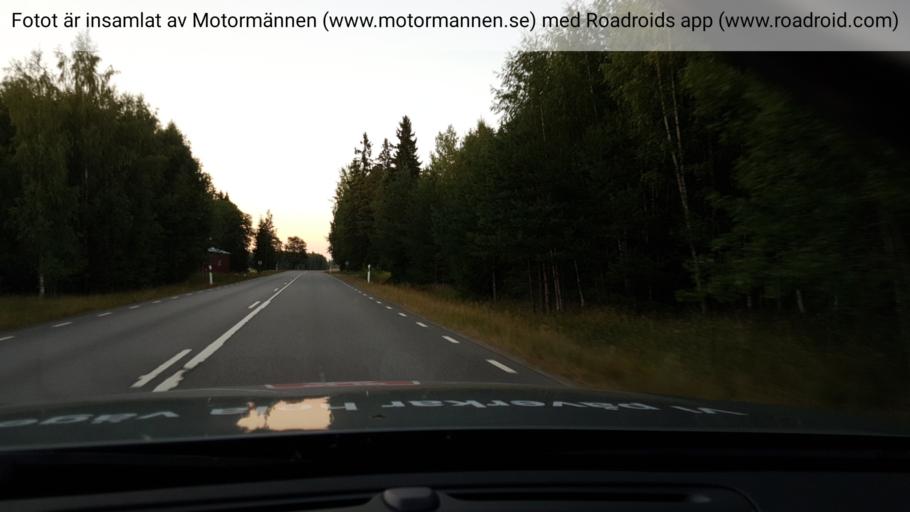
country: SE
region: Uppsala
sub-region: Heby Kommun
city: OEstervala
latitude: 60.1090
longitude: 17.2073
